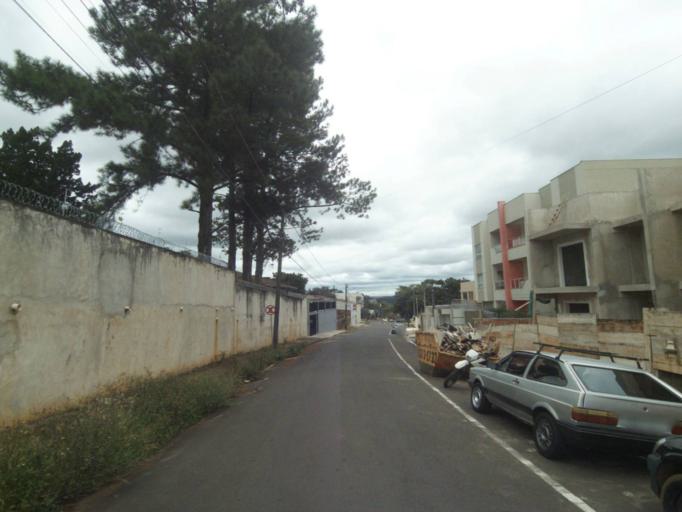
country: BR
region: Parana
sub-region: Telemaco Borba
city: Telemaco Borba
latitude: -24.3318
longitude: -50.6122
